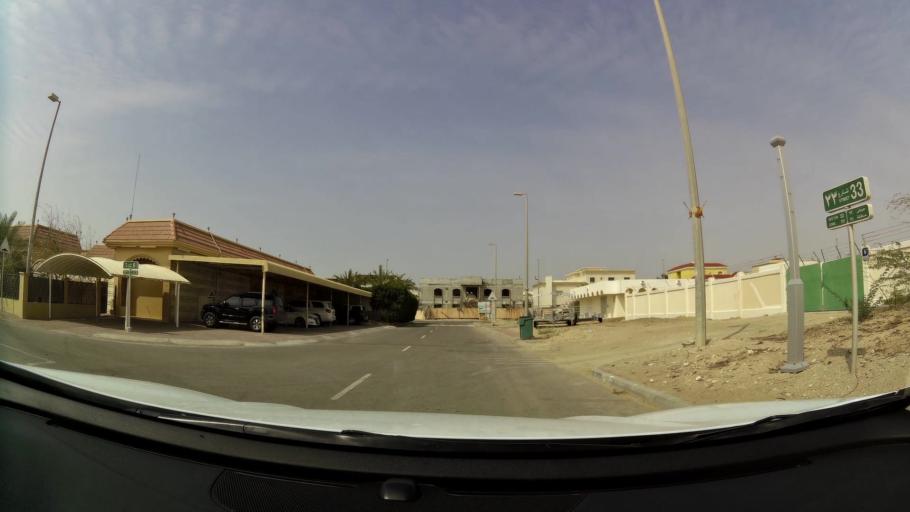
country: AE
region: Abu Dhabi
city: Abu Dhabi
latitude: 24.5449
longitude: 54.6830
